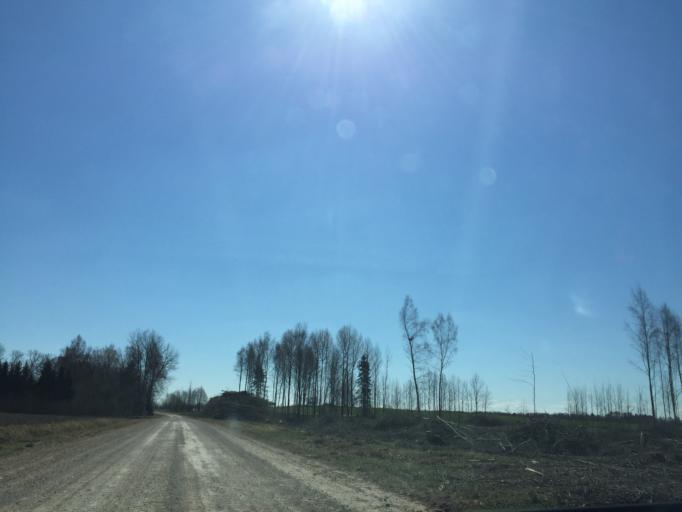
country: EE
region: Viljandimaa
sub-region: Viiratsi vald
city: Viiratsi
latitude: 58.3629
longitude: 25.7522
